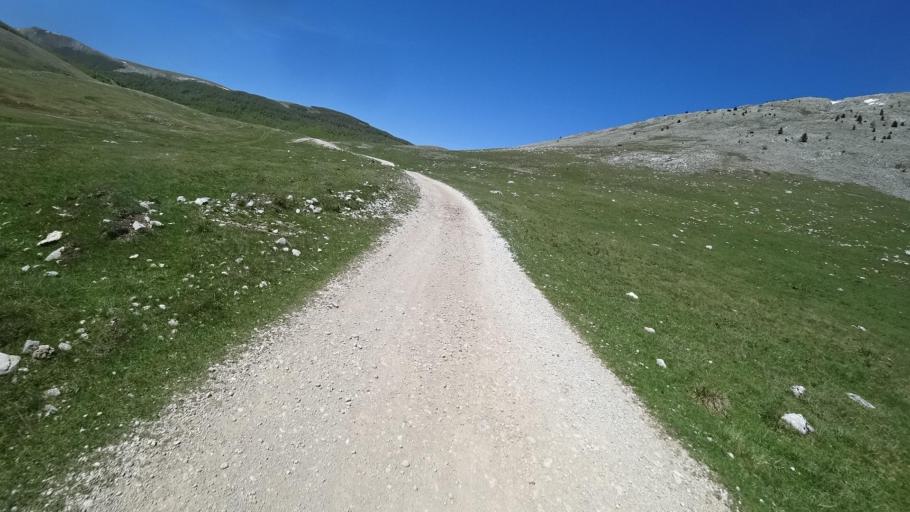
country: BA
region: Federation of Bosnia and Herzegovina
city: Pazaric
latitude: 43.6685
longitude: 18.1794
